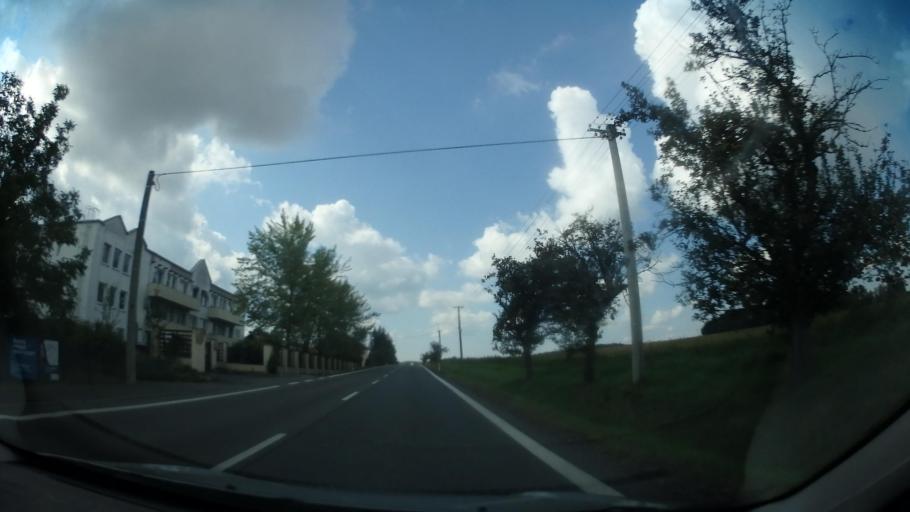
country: CZ
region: Central Bohemia
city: Kostelec nad Cernymi Lesy
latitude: 49.9729
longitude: 14.9112
